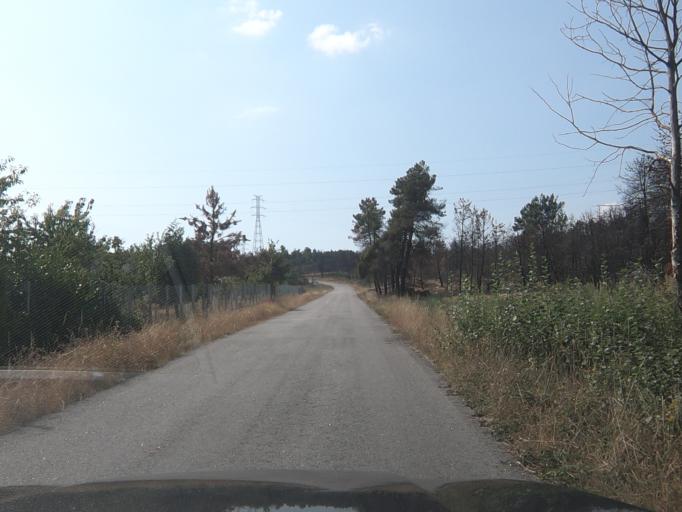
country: PT
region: Vila Real
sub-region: Sabrosa
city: Sabrosa
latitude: 41.3297
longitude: -7.6154
